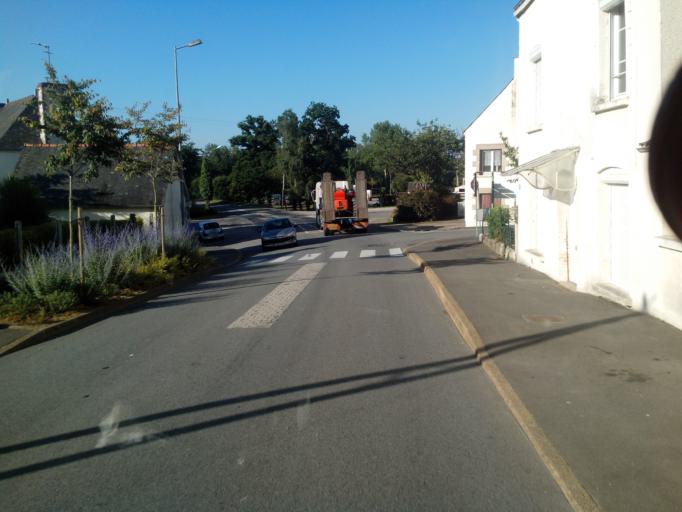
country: FR
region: Brittany
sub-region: Departement du Morbihan
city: Loyat
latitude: 47.9867
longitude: -2.3802
